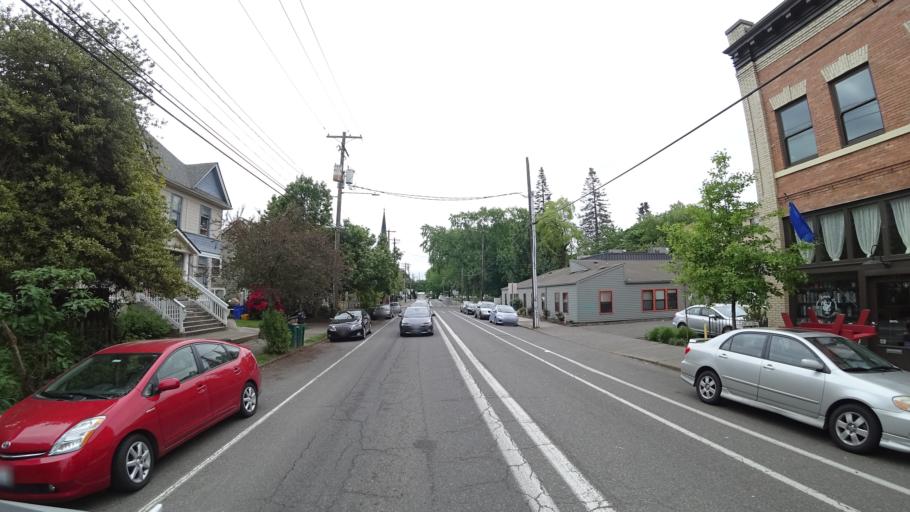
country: US
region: Oregon
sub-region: Multnomah County
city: Portland
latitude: 45.5452
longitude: -122.6667
